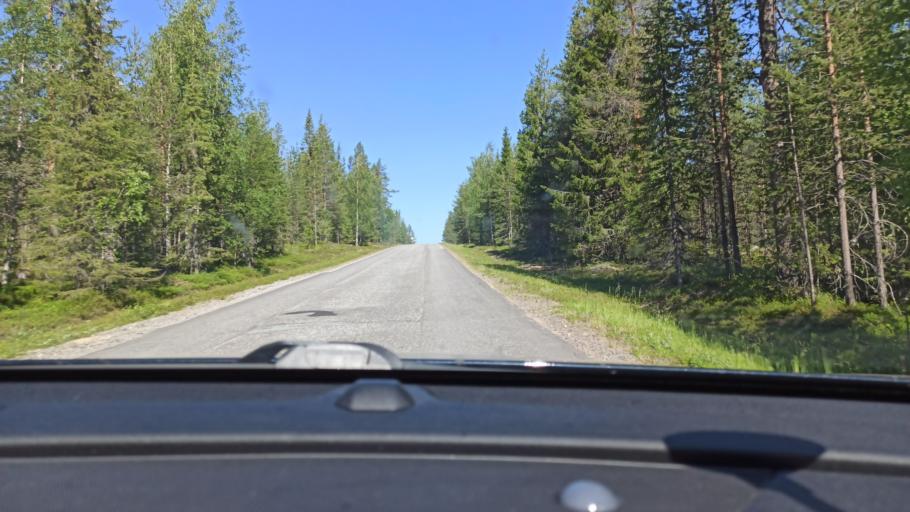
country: FI
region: Lapland
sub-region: Tunturi-Lappi
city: Kolari
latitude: 67.6788
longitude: 24.1405
